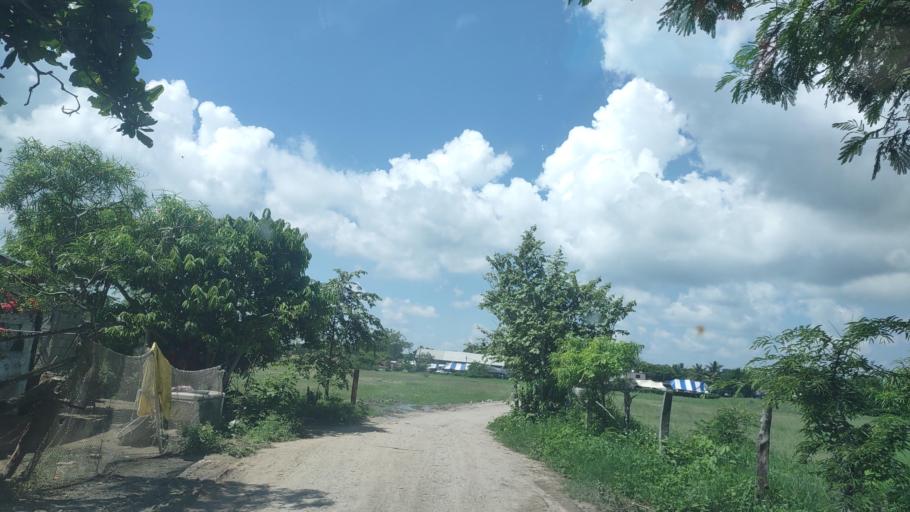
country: MX
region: Veracruz
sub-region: Ozuluama de Mascarenas
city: Cucharas
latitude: 21.6170
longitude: -97.6581
